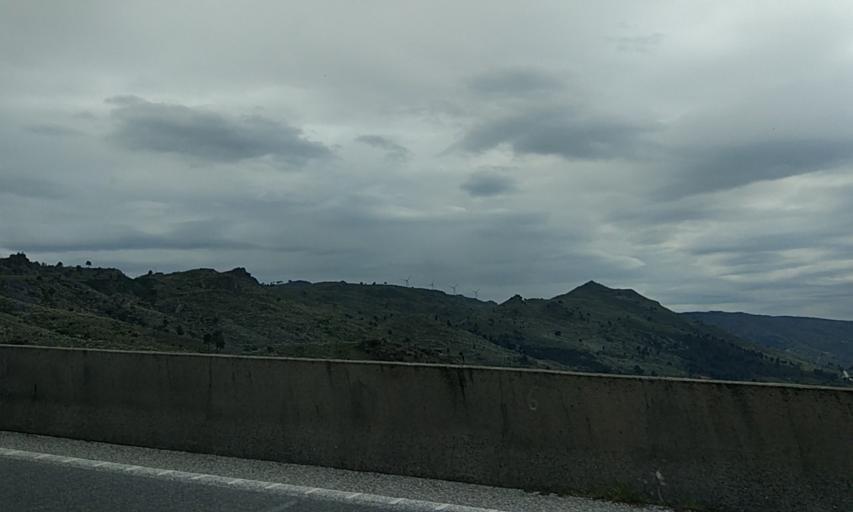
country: PT
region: Guarda
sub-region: Guarda
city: Guarda
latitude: 40.6018
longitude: -7.2800
